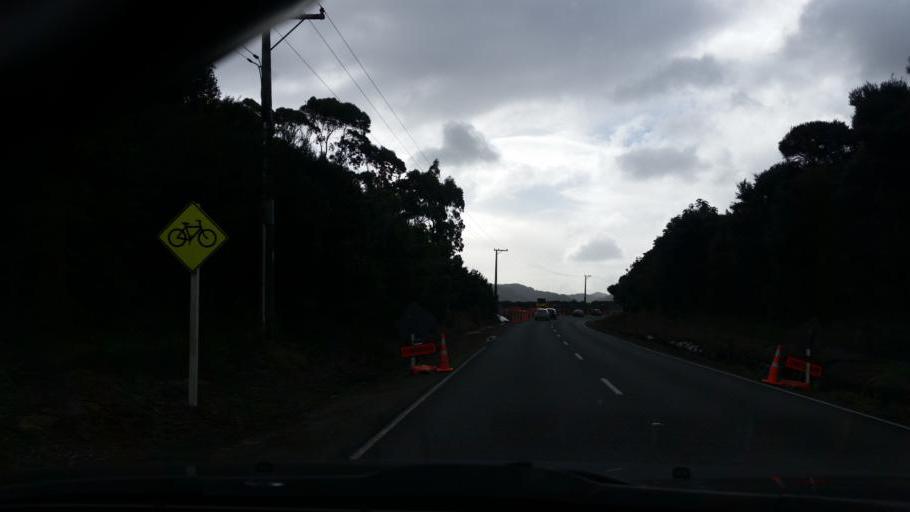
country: NZ
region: Auckland
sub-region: Auckland
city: Wellsford
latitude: -36.1143
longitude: 174.5750
